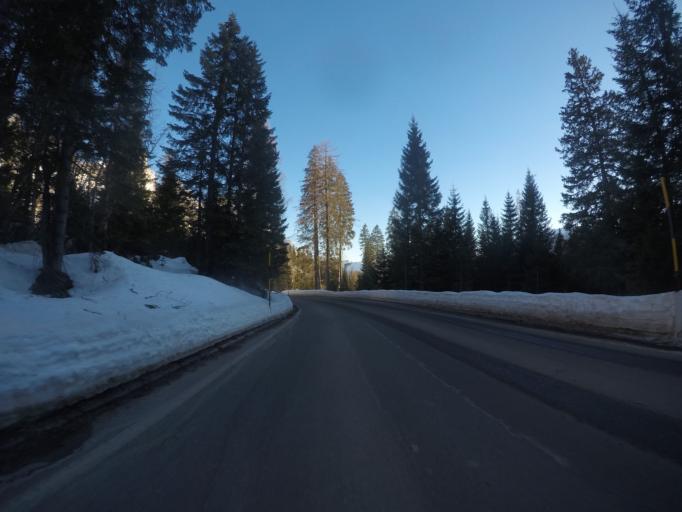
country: IT
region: Trentino-Alto Adige
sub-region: Provincia di Trento
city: Siror
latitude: 46.2763
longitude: 11.7997
